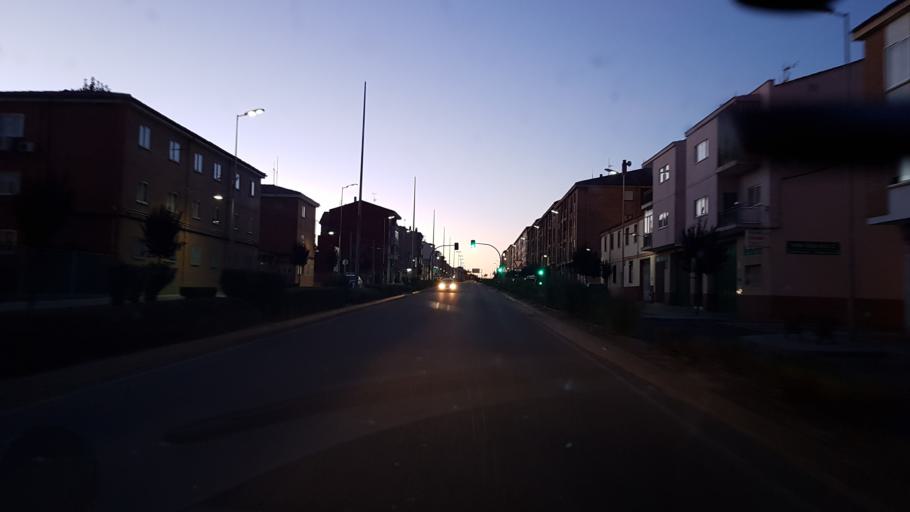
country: ES
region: Castille and Leon
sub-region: Provincia de Zamora
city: Toro
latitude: 41.5267
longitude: -5.3967
